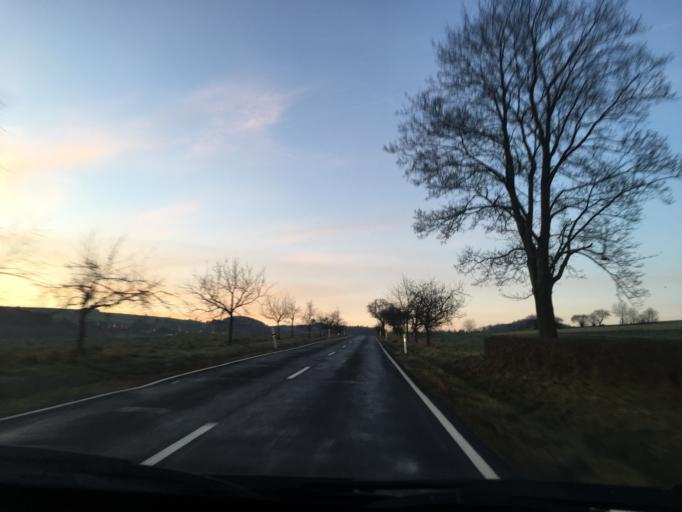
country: DE
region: Hesse
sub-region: Regierungsbezirk Kassel
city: Hofbieber
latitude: 50.6171
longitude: 9.9013
